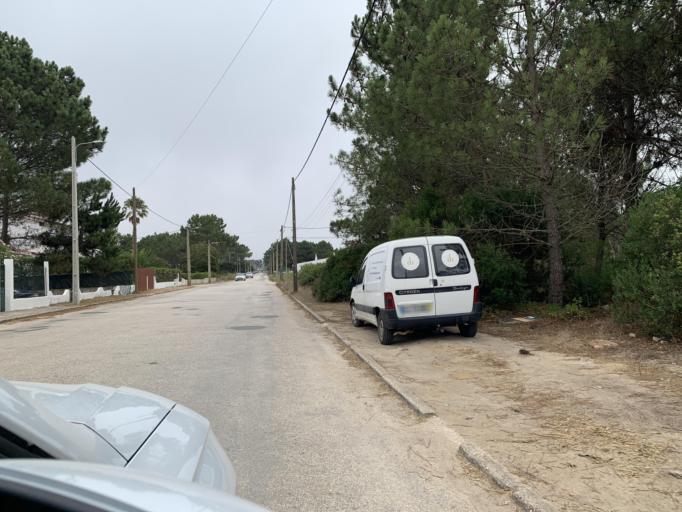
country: PT
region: Faro
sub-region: Aljezur
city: Aljezur
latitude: 37.3100
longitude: -8.8534
